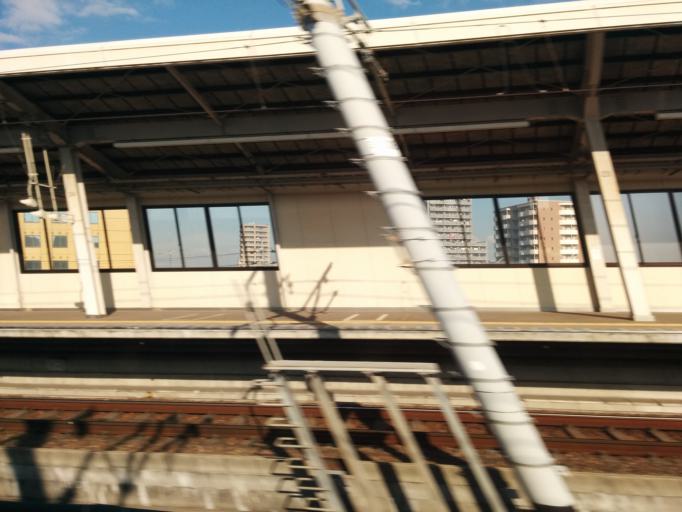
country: JP
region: Aichi
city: Anjo
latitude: 34.9698
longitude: 137.0598
